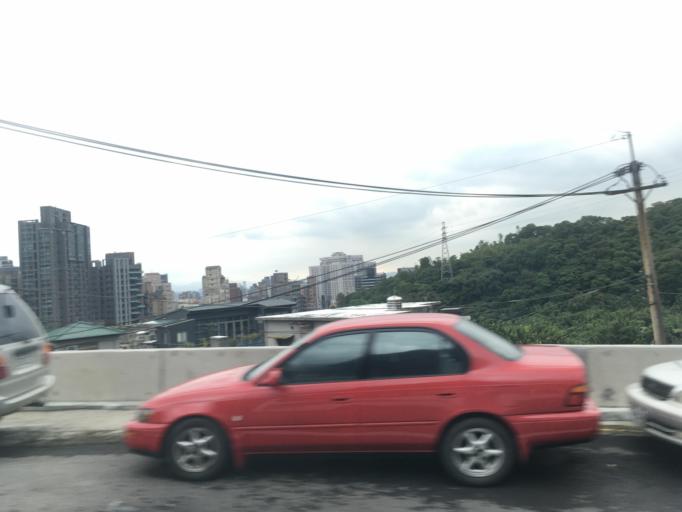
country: TW
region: Taipei
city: Taipei
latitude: 25.1278
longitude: 121.5283
